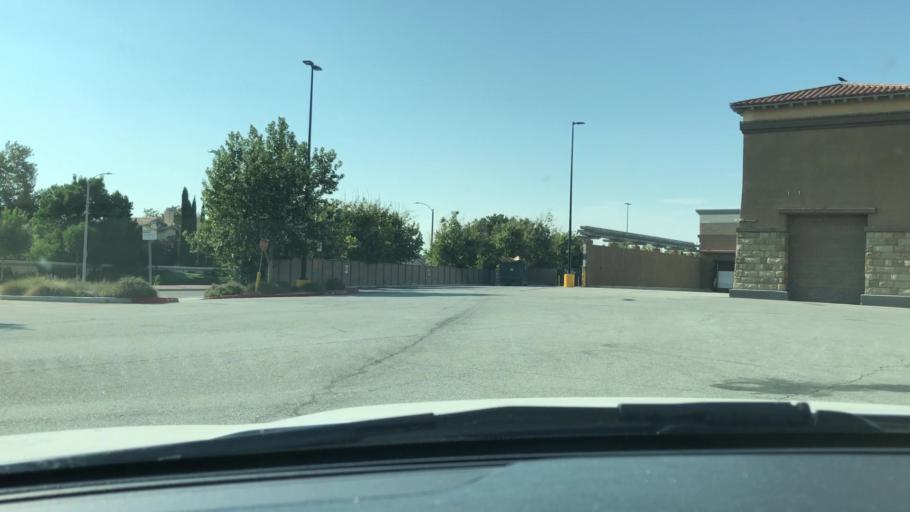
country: US
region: California
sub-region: Los Angeles County
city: Lancaster
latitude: 34.6925
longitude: -118.1744
